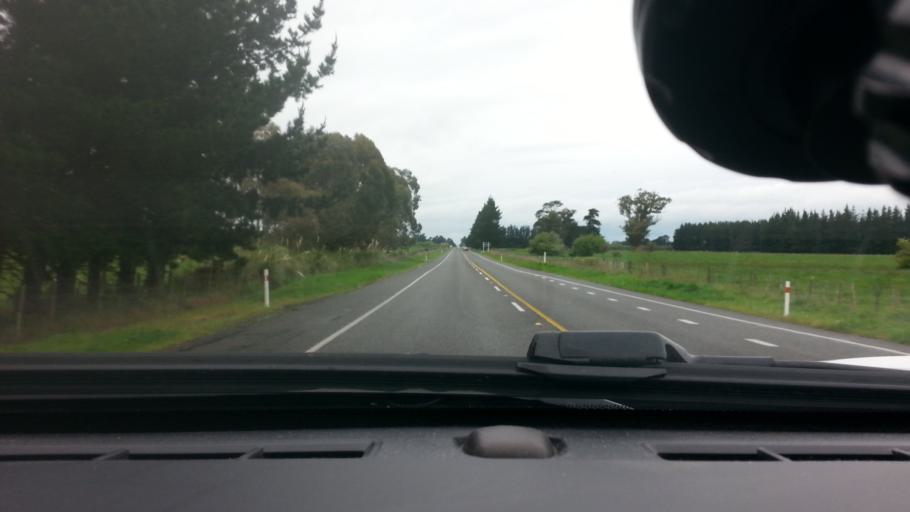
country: NZ
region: Wellington
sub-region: Masterton District
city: Masterton
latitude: -41.1140
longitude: 175.3894
